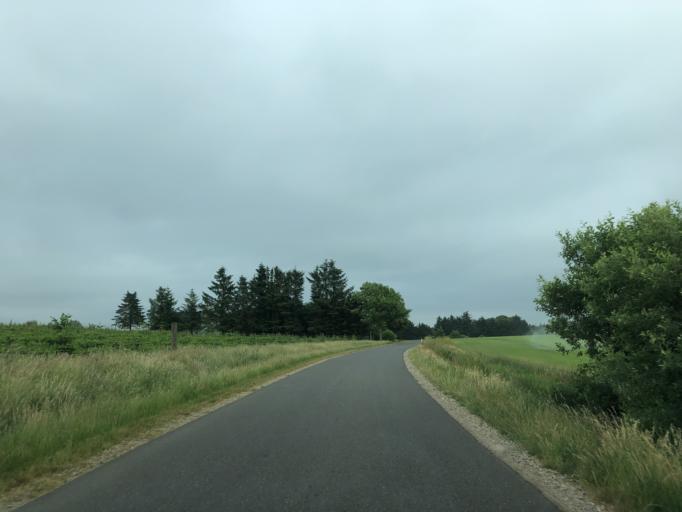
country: DK
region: Central Jutland
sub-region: Holstebro Kommune
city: Holstebro
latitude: 56.2560
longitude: 8.5692
